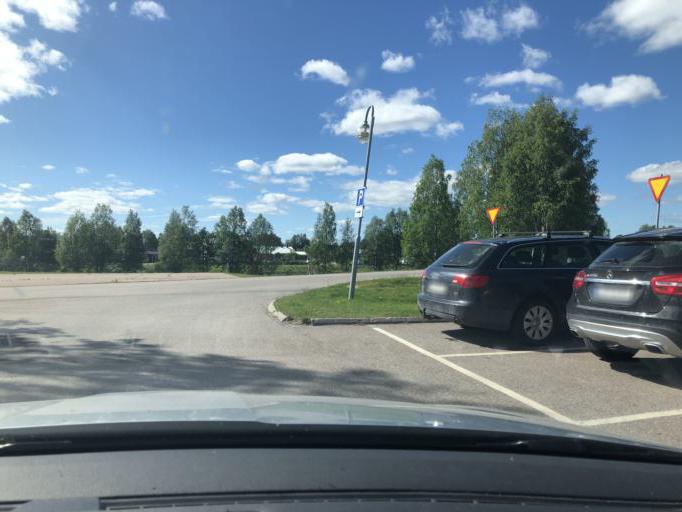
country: SE
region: Norrbotten
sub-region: Gallivare Kommun
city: Gaellivare
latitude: 67.1312
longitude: 20.6841
